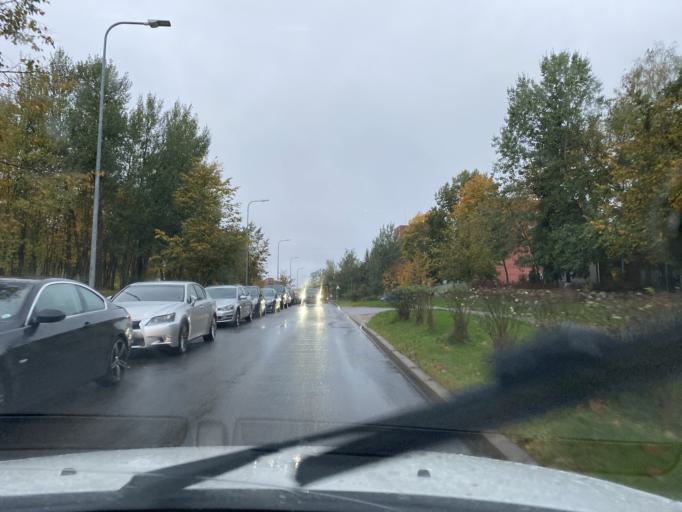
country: LT
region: Vilnius County
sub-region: Vilnius
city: Fabijoniskes
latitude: 54.7429
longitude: 25.2693
